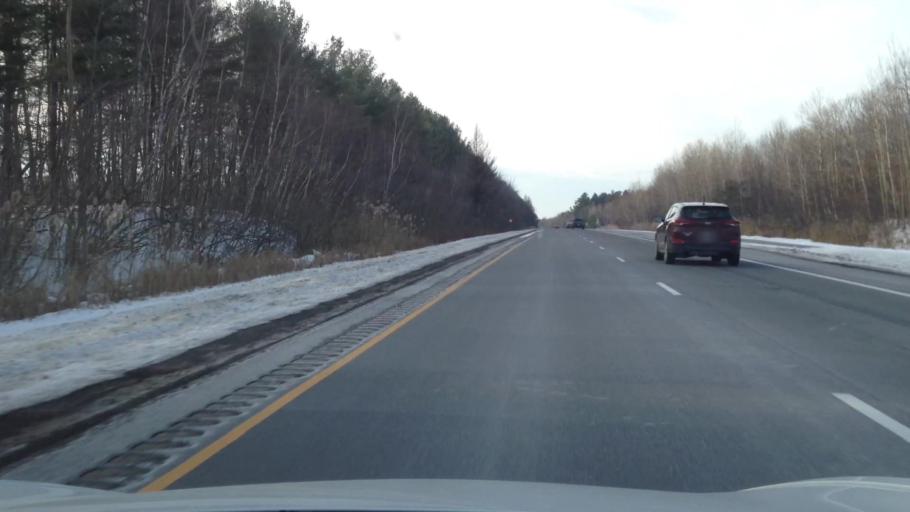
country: CA
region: Quebec
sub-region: Laurentides
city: Brownsburg-Chatham
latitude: 45.5553
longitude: -74.4561
